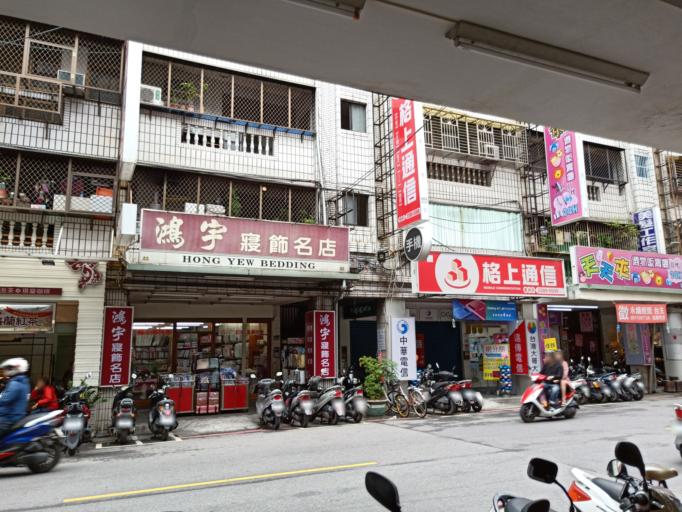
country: TW
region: Taipei
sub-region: Taipei
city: Banqiao
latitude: 25.0812
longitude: 121.4627
